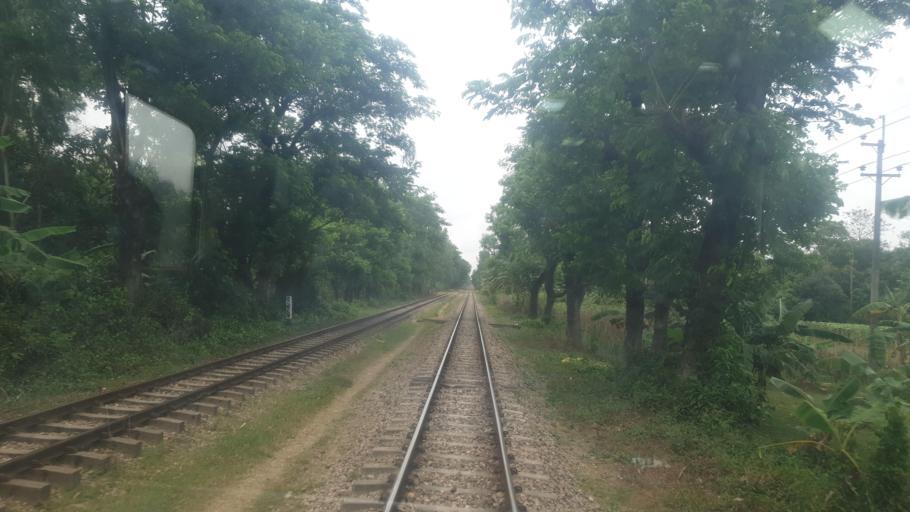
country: BD
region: Chittagong
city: Fatikchari
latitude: 22.6436
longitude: 91.6508
